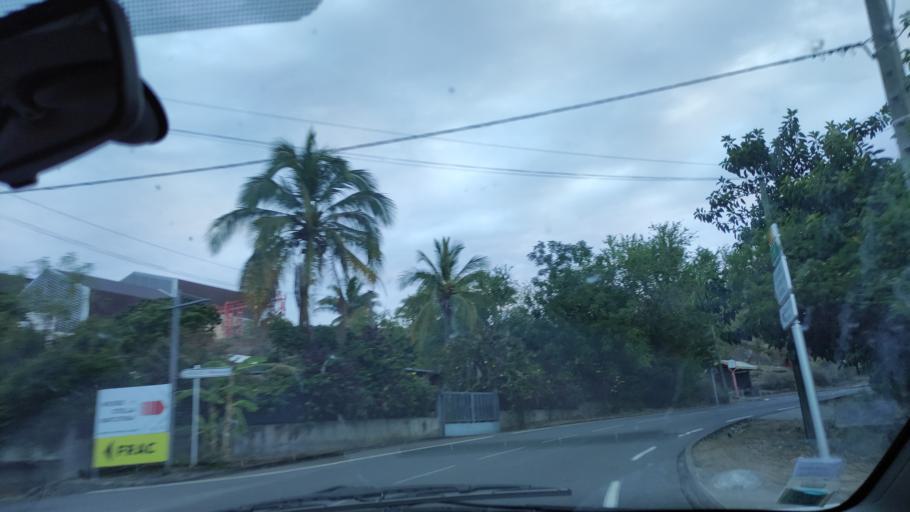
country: RE
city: Piton Saint-Leu
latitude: -21.2017
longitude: 55.2944
